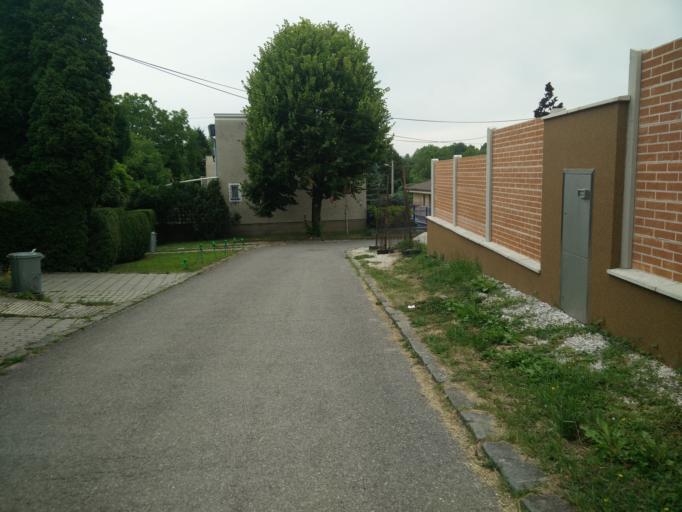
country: SK
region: Nitriansky
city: Bojnice
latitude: 48.7780
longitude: 18.5851
